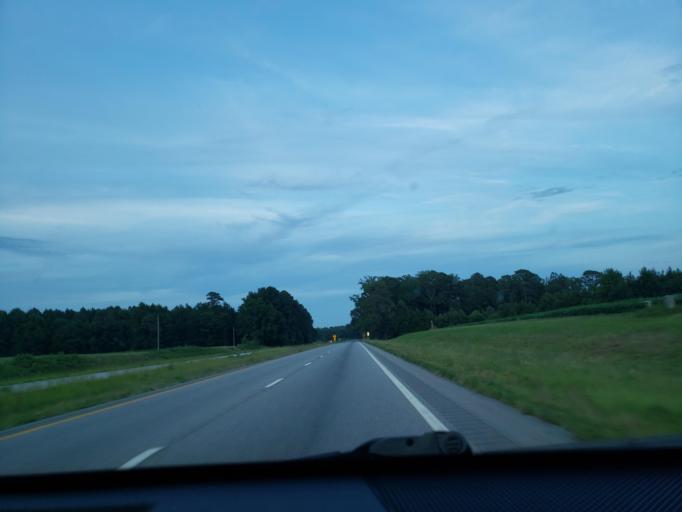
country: US
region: Virginia
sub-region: Southampton County
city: Courtland
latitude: 36.7069
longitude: -77.1744
